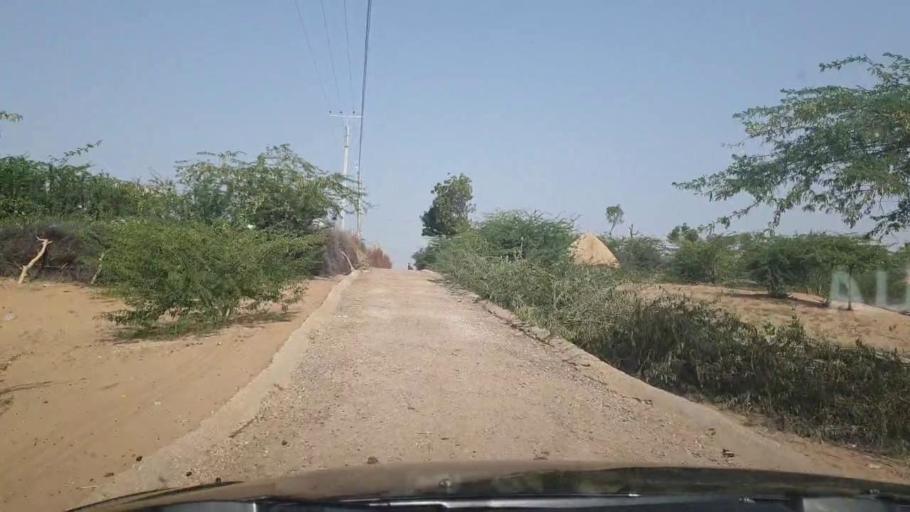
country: PK
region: Sindh
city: Islamkot
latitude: 25.0077
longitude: 70.2105
